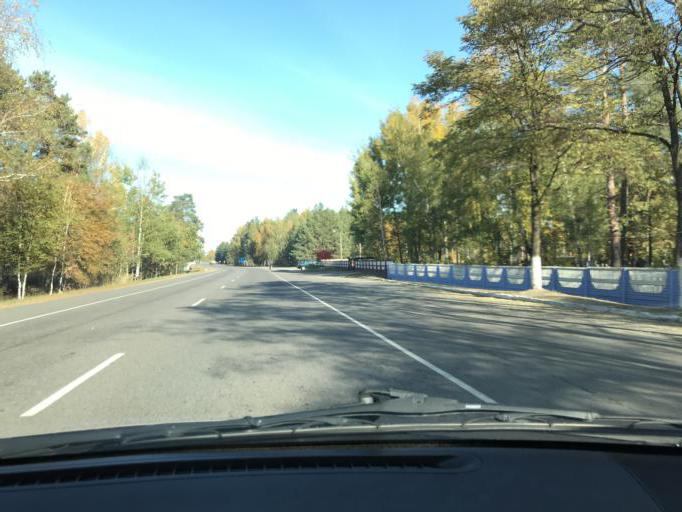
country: BY
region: Brest
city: Mikashevichy
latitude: 52.2360
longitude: 27.4485
